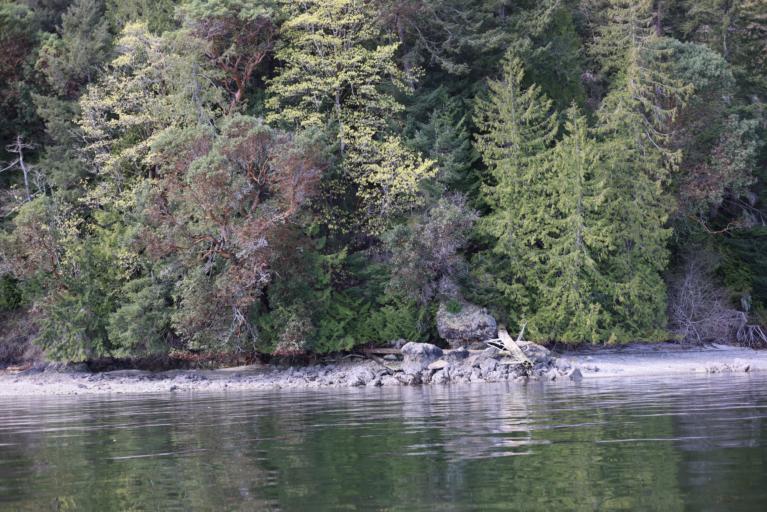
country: CA
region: British Columbia
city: North Saanich
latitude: 48.5954
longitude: -123.5212
